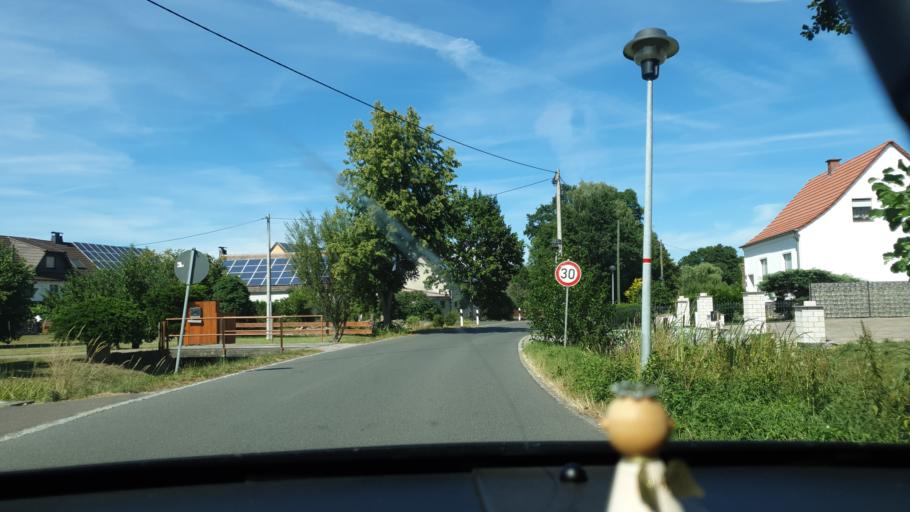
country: DE
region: Saxony
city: Mockrehna
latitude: 51.4958
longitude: 12.8374
